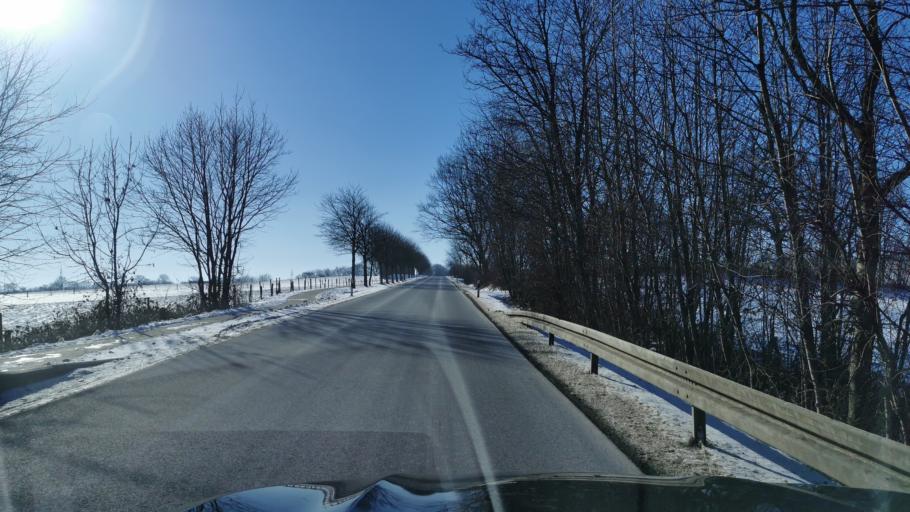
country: DE
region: Schleswig-Holstein
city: Grundhof
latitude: 54.7676
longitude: 9.6456
